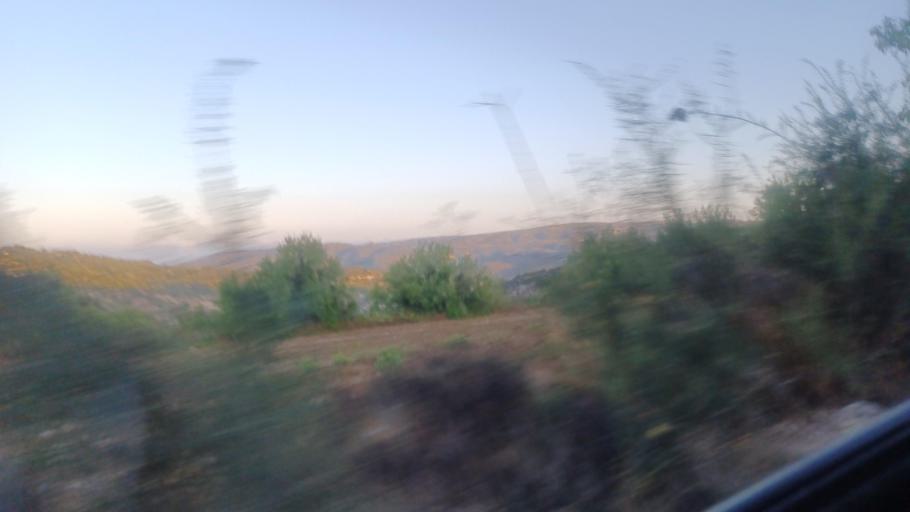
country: CY
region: Pafos
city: Tala
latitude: 34.8594
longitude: 32.4687
